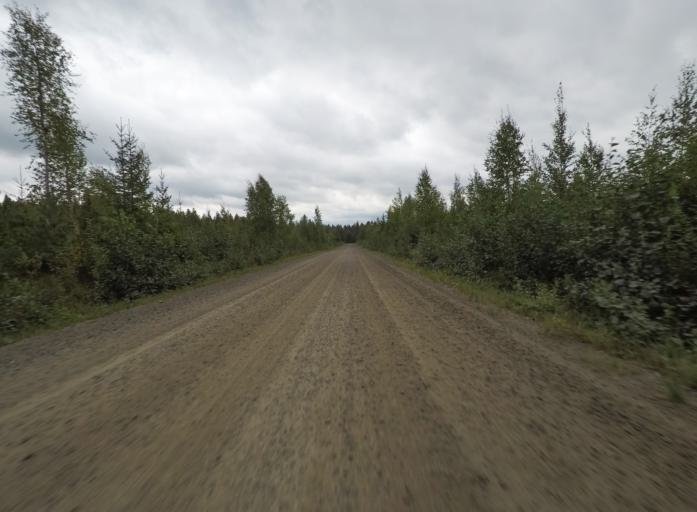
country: FI
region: Central Finland
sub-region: Jyvaeskylae
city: Hankasalmi
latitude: 62.4080
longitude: 26.6041
